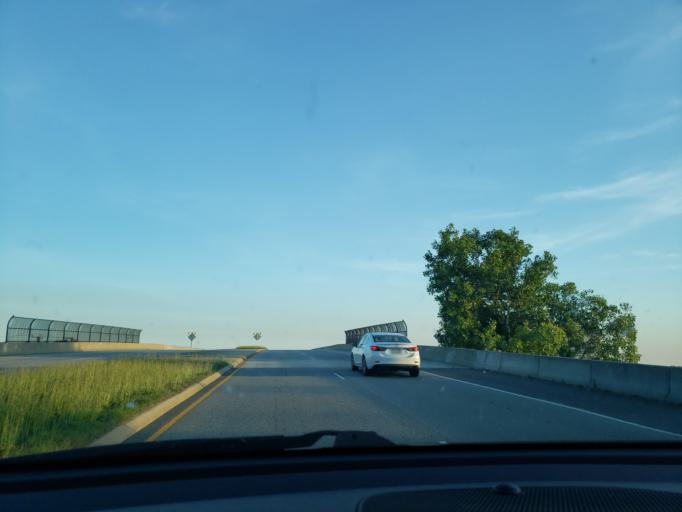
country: US
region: Virginia
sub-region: Henrico County
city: Fort Lee
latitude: 37.4973
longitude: -77.3408
